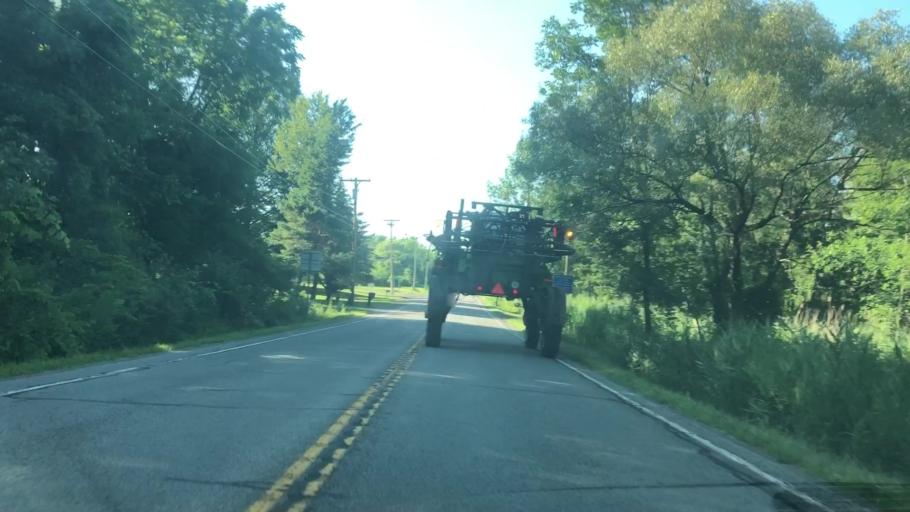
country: US
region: New York
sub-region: Wayne County
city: Ontario
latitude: 43.1972
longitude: -77.2959
